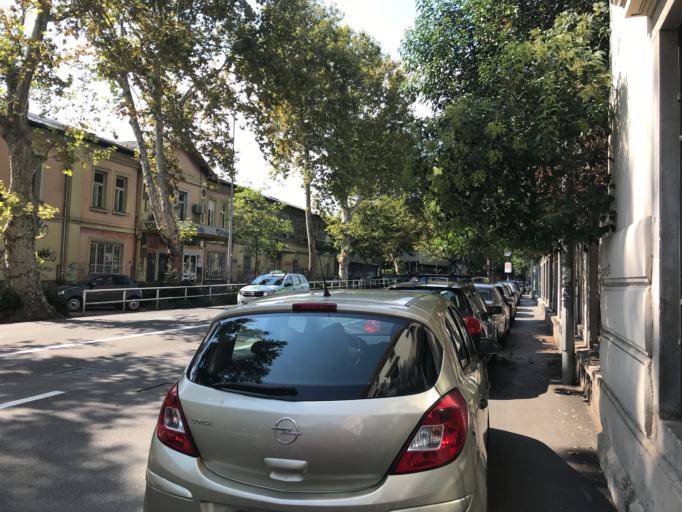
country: HR
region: Primorsko-Goranska
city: Drenova
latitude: 45.3310
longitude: 14.4283
